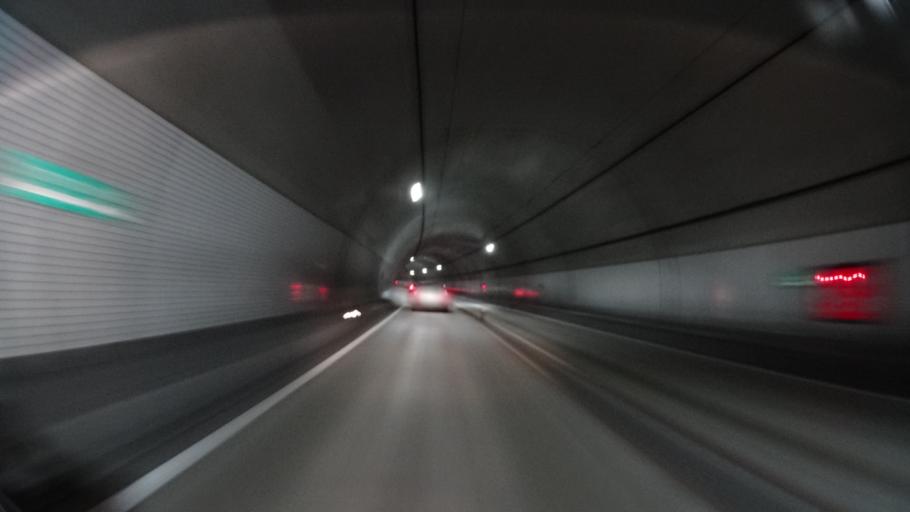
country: JP
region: Gunma
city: Numata
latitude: 36.6606
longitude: 139.1660
